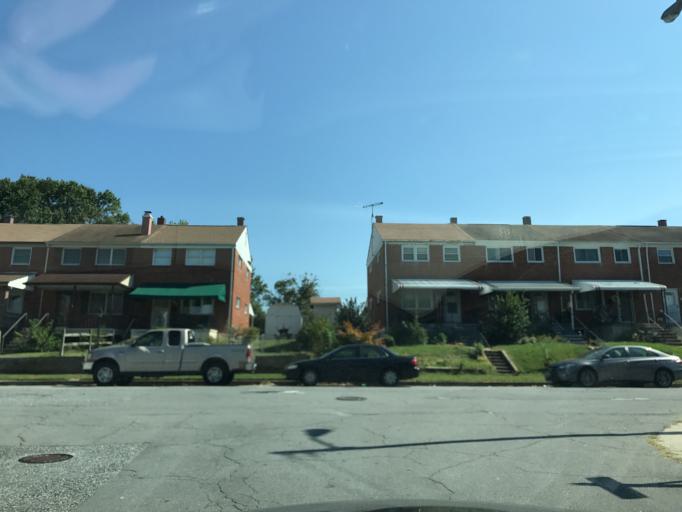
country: US
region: Maryland
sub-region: Baltimore County
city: Middle River
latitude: 39.3114
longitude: -76.4490
